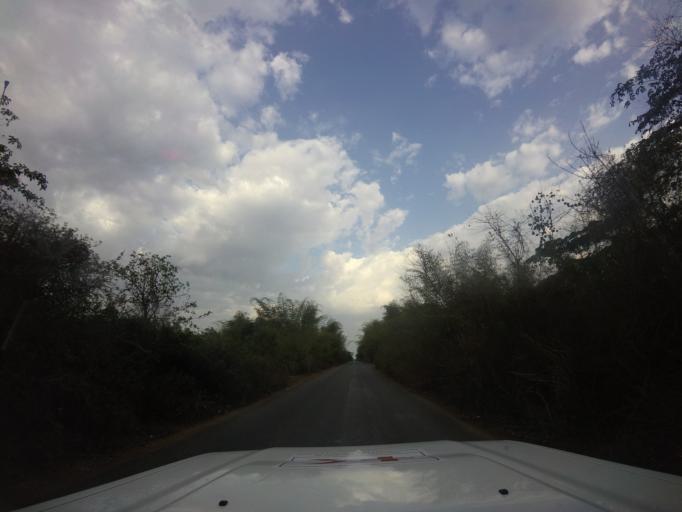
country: LR
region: Bomi
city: Tubmanburg
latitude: 6.6885
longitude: -10.8794
